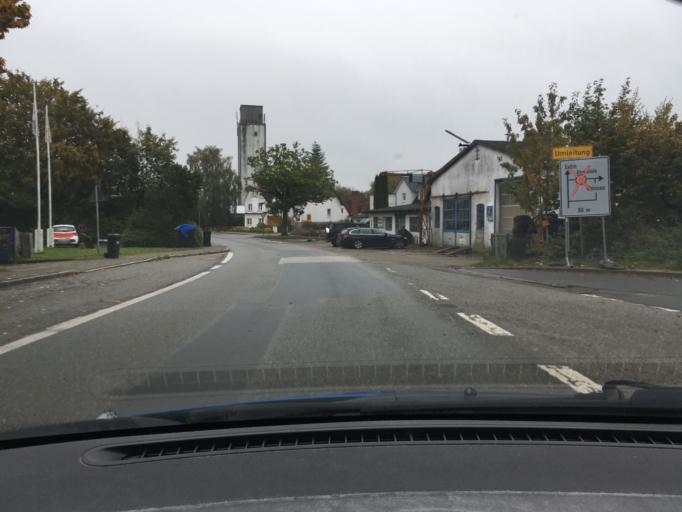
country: DE
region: Schleswig-Holstein
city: Bosau
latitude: 54.0896
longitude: 10.4744
